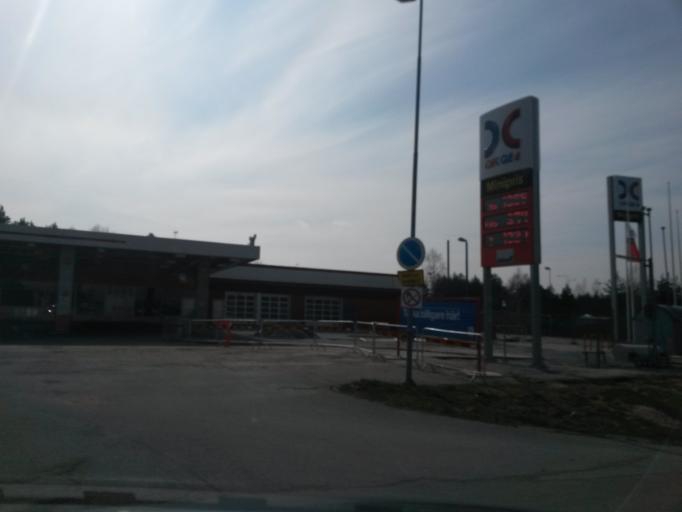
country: SE
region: OErebro
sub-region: Kumla Kommun
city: Kumla
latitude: 59.2153
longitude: 15.1364
